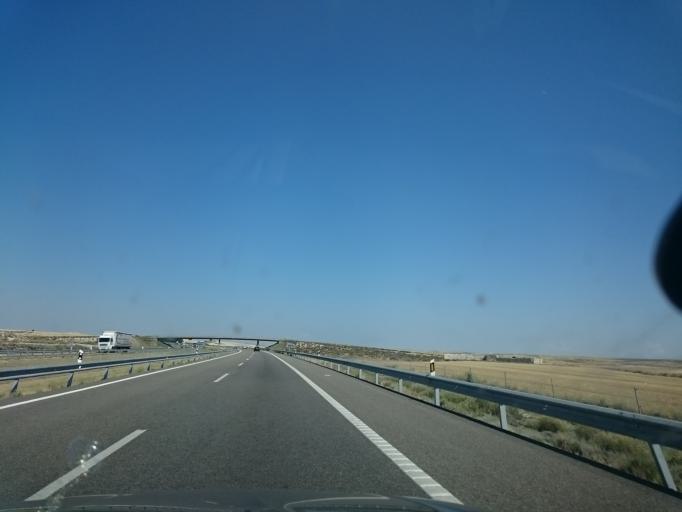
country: ES
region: Aragon
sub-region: Provincia de Zaragoza
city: Bujaraloz
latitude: 41.5177
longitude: -0.2328
